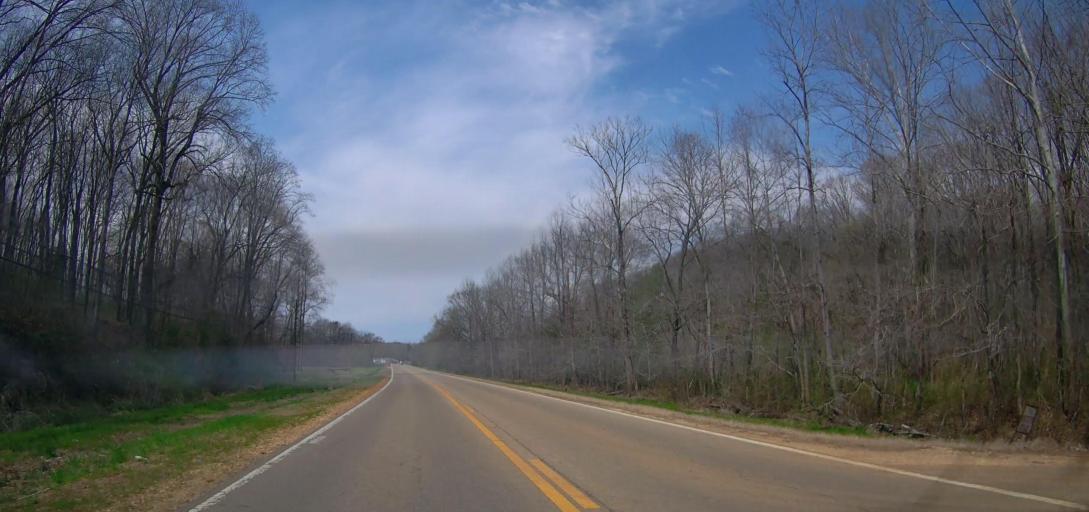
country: US
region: Mississippi
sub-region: Union County
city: New Albany
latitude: 34.4674
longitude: -88.9857
